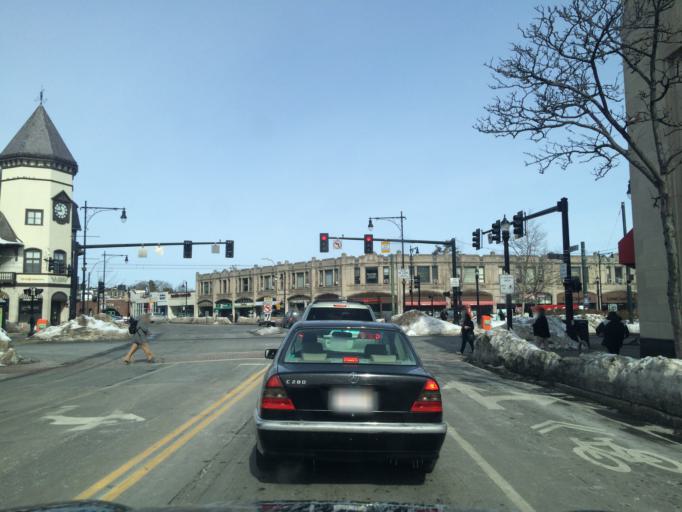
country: US
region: Massachusetts
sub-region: Norfolk County
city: Brookline
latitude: 42.3417
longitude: -71.1211
